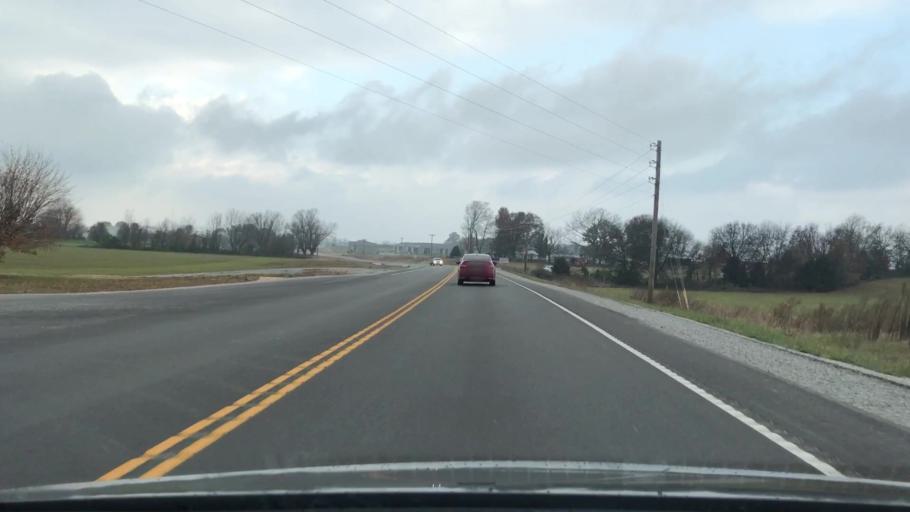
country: US
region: Kentucky
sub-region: Simpson County
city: Franklin
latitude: 36.7125
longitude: -86.5046
